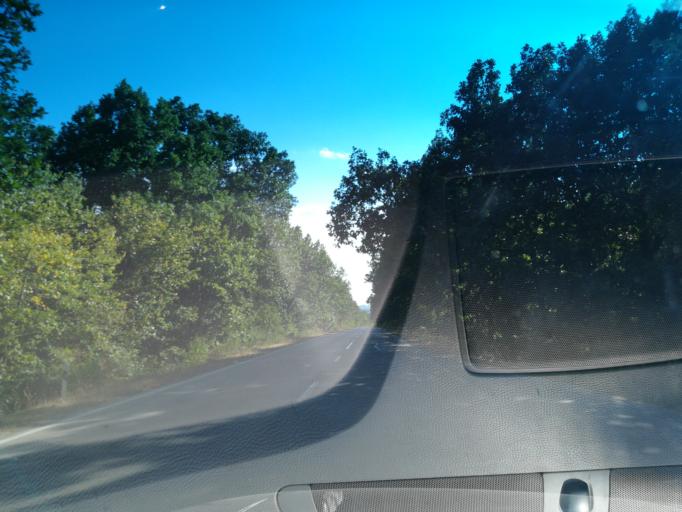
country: BG
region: Khaskovo
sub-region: Obshtina Mineralni Bani
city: Mineralni Bani
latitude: 41.9936
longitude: 25.3609
